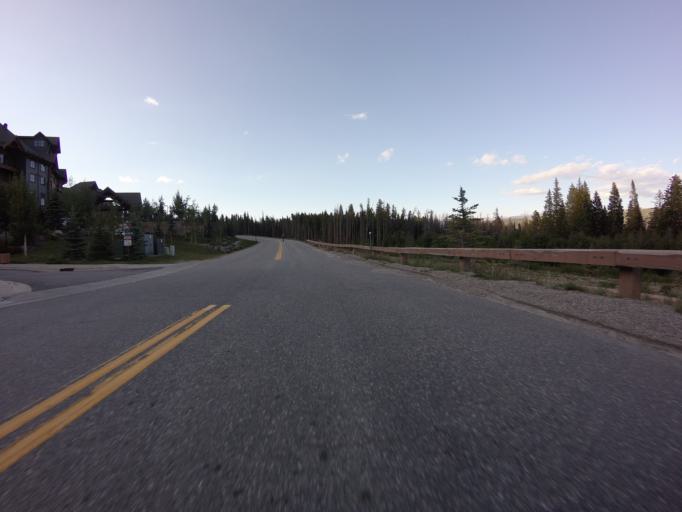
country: US
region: Colorado
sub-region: Summit County
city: Breckenridge
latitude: 39.4856
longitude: -106.0663
